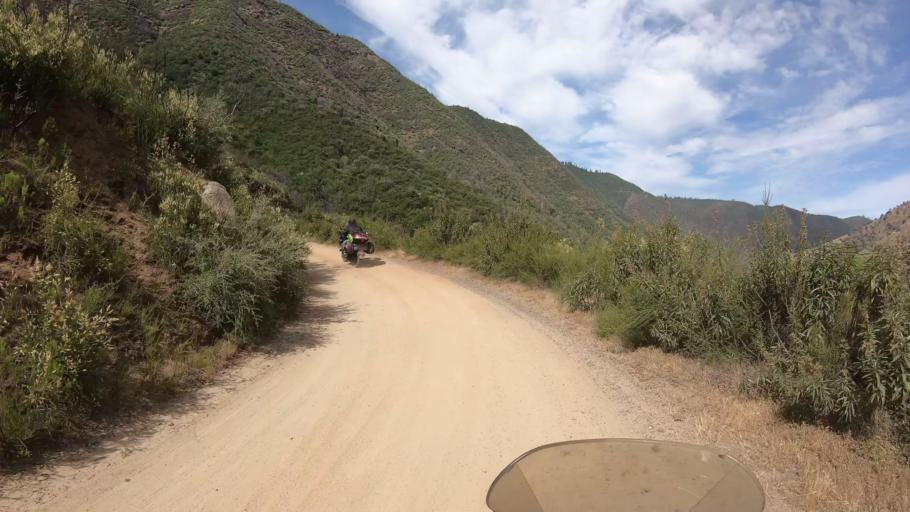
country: US
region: California
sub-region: Tuolumne County
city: Tuolumne City
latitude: 37.8371
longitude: -120.0748
